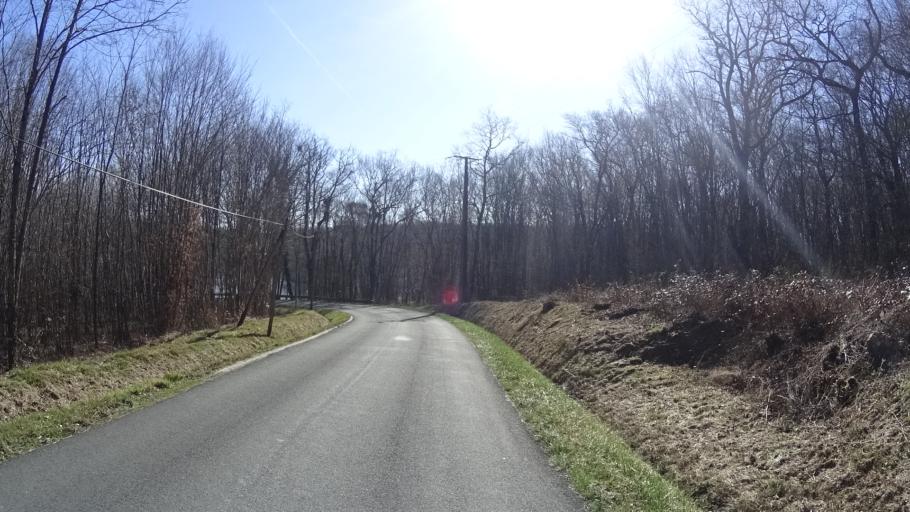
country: FR
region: Aquitaine
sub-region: Departement de la Dordogne
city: Saint-Aulaye
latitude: 45.1285
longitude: 0.2401
